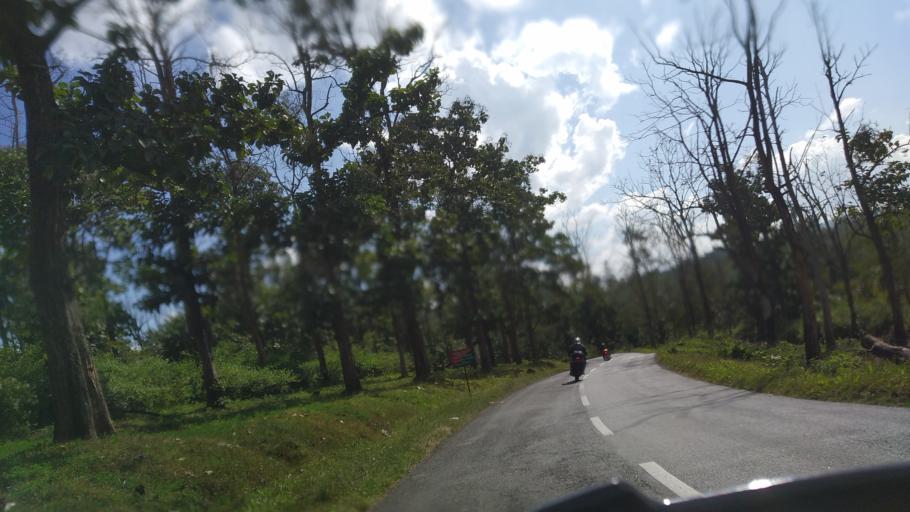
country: IN
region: Kerala
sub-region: Wayanad
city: Panamaram
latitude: 11.9152
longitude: 76.0632
